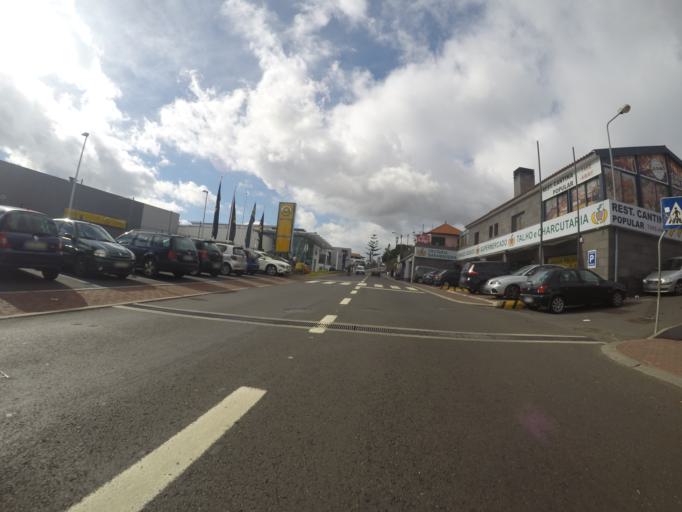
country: PT
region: Madeira
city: Camara de Lobos
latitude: 32.6565
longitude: -16.9432
